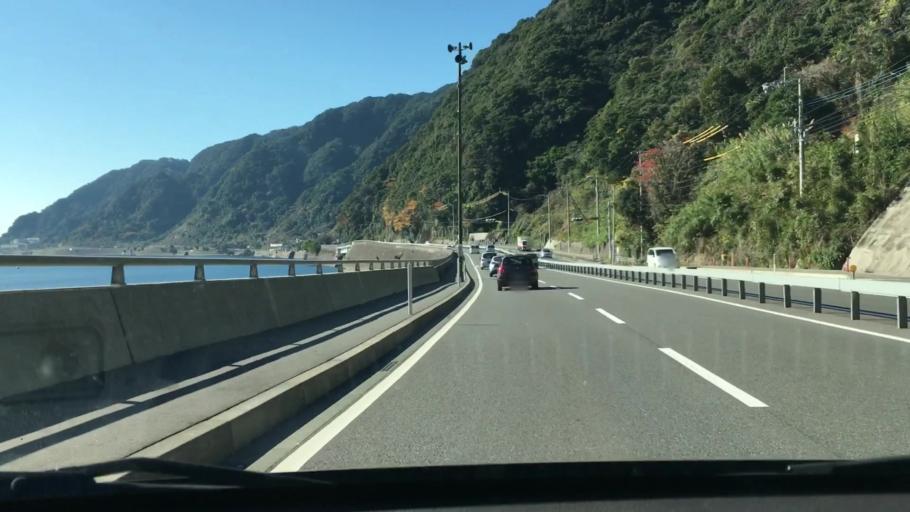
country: JP
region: Kagoshima
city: Kajiki
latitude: 31.6547
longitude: 130.6103
